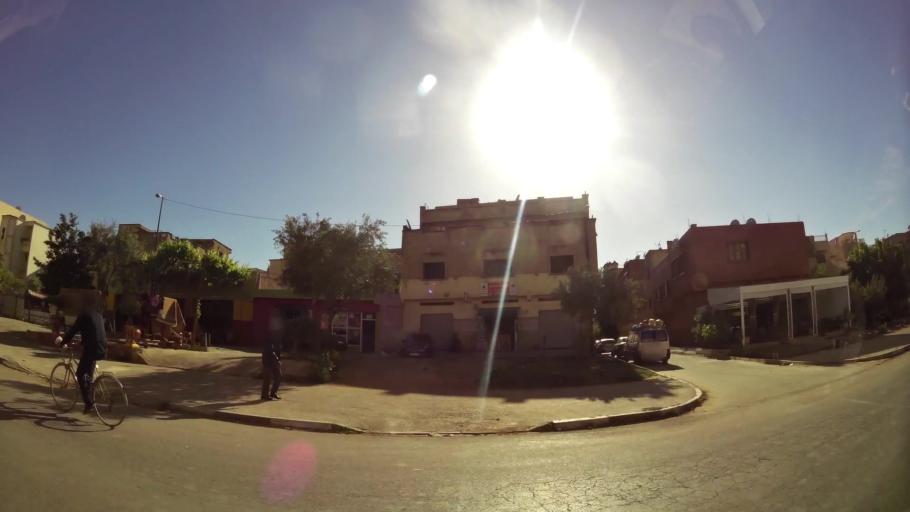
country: MA
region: Meknes-Tafilalet
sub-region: Meknes
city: Meknes
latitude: 33.8894
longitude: -5.4998
